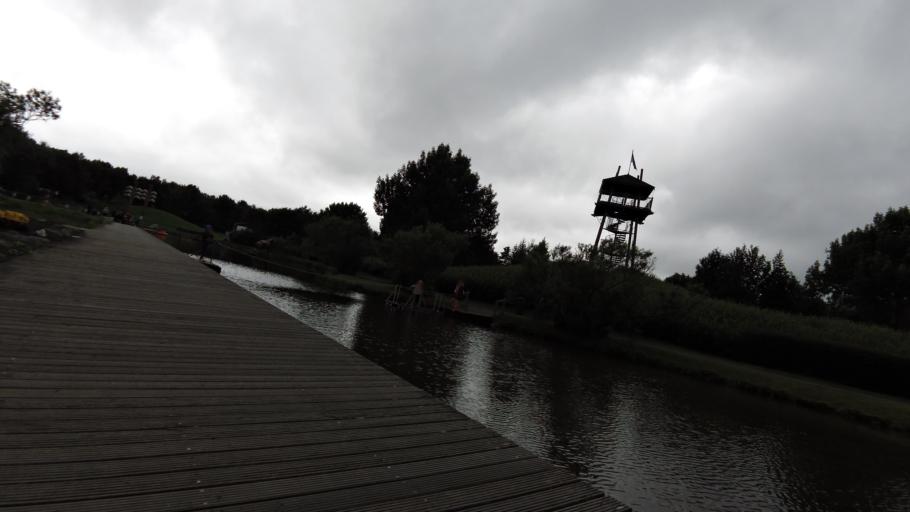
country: IS
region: Capital Region
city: Reykjavik
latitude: 64.1381
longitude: -21.8682
